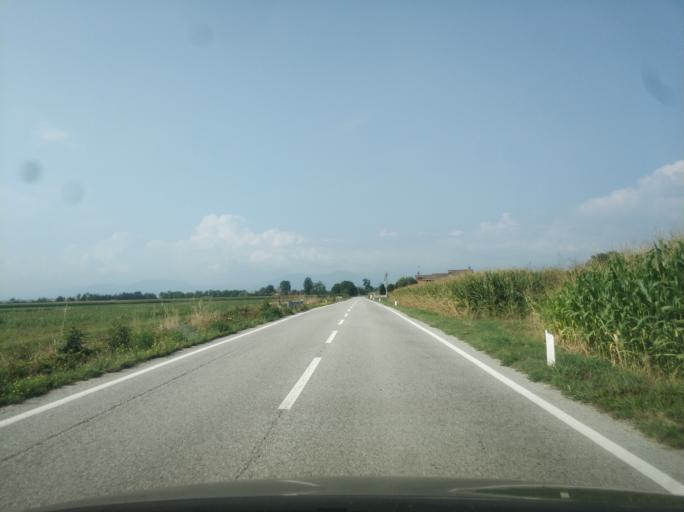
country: IT
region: Piedmont
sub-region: Provincia di Cuneo
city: Tarantasca
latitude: 44.4827
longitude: 7.5385
